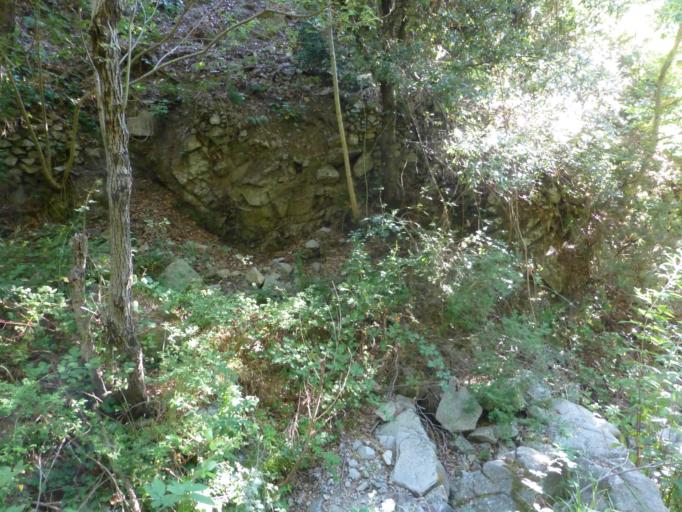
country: IT
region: Calabria
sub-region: Provincia di Reggio Calabria
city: Bivongi
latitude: 38.4996
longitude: 16.4276
